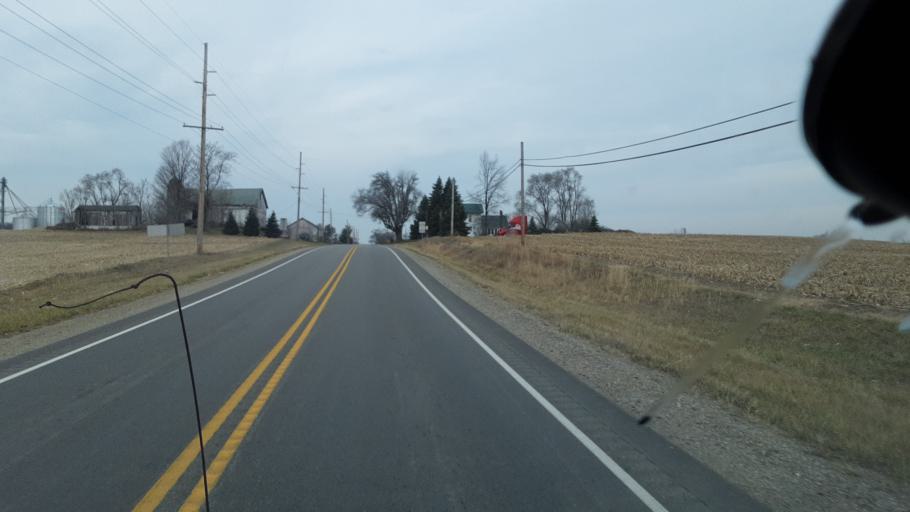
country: US
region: Indiana
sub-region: Noble County
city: Kendallville
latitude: 41.5275
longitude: -85.1706
